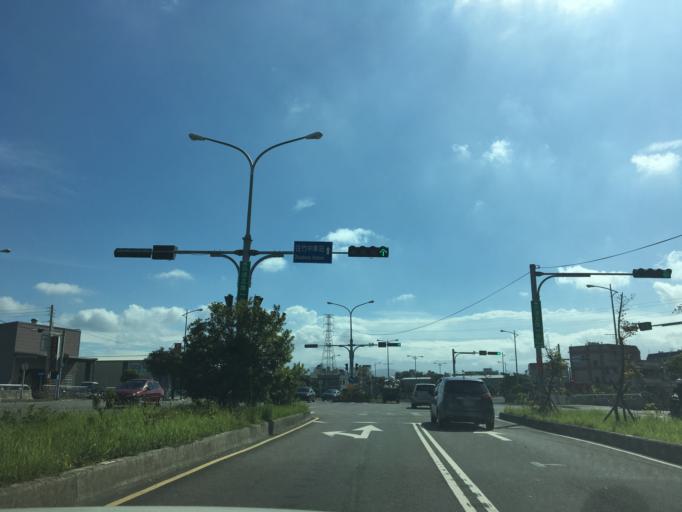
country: TW
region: Taiwan
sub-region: Hsinchu
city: Zhubei
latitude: 24.7943
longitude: 121.0202
